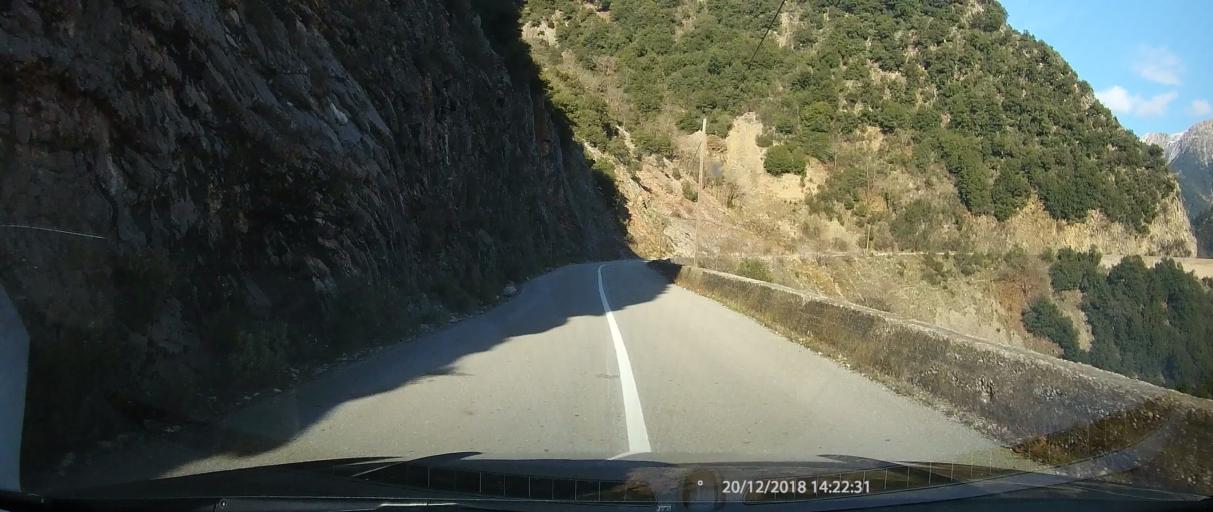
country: GR
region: West Greece
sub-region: Nomos Aitolias kai Akarnanias
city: Thermo
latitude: 38.7525
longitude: 21.6642
